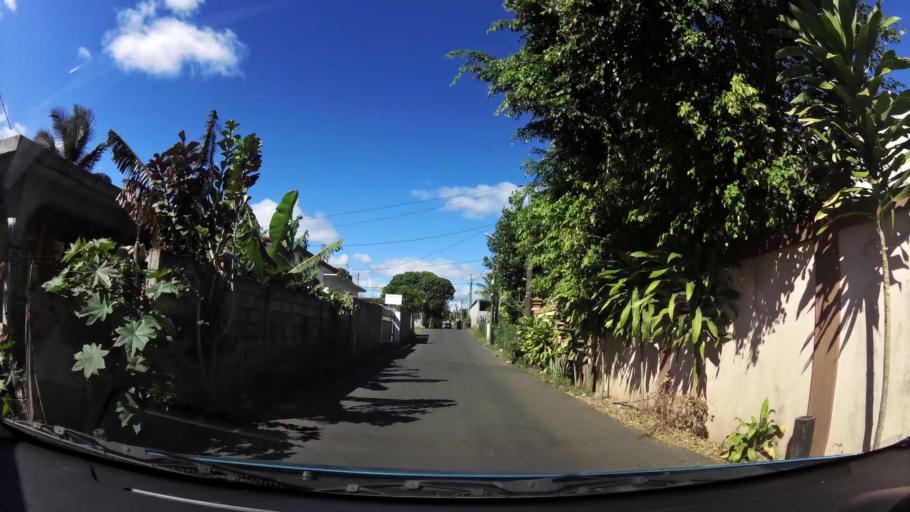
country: MU
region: Plaines Wilhems
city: Vacoas
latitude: -20.2826
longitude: 57.4631
